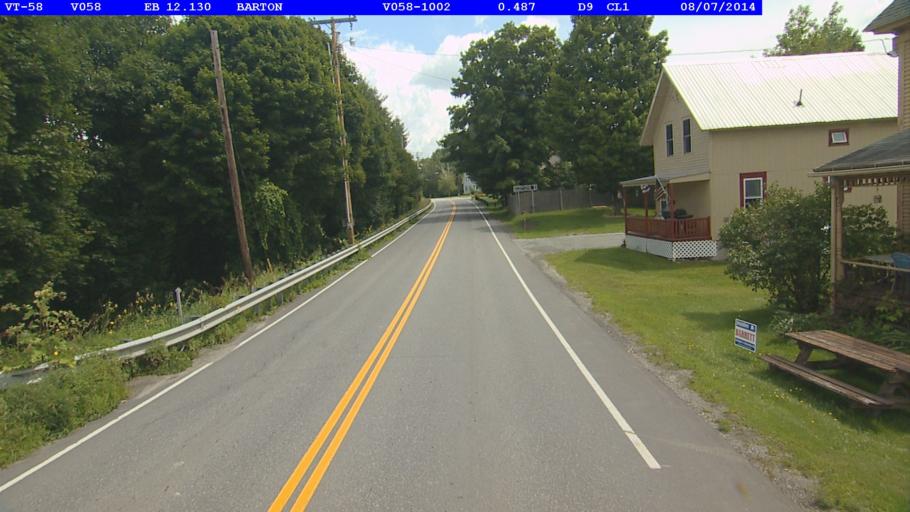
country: US
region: Vermont
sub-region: Orleans County
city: Newport
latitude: 44.8111
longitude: -72.2004
